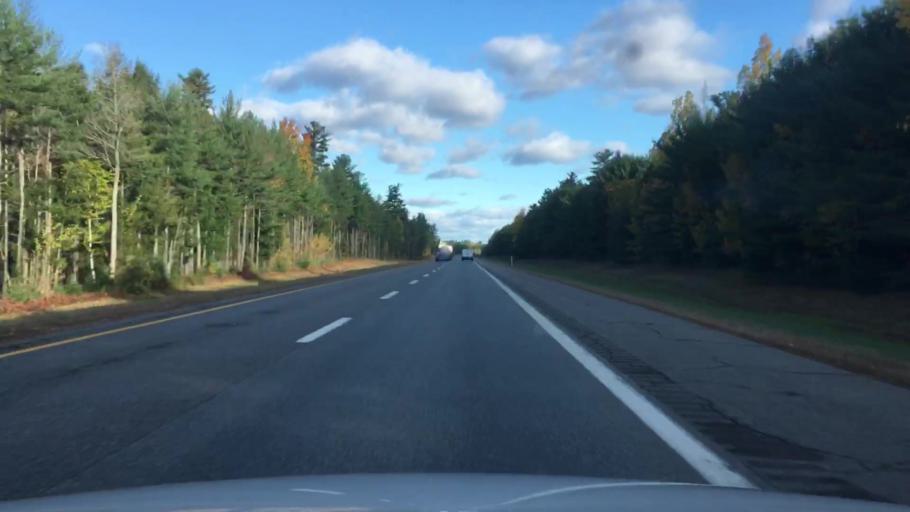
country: US
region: Maine
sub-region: Penobscot County
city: Greenbush
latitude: 45.1373
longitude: -68.6992
